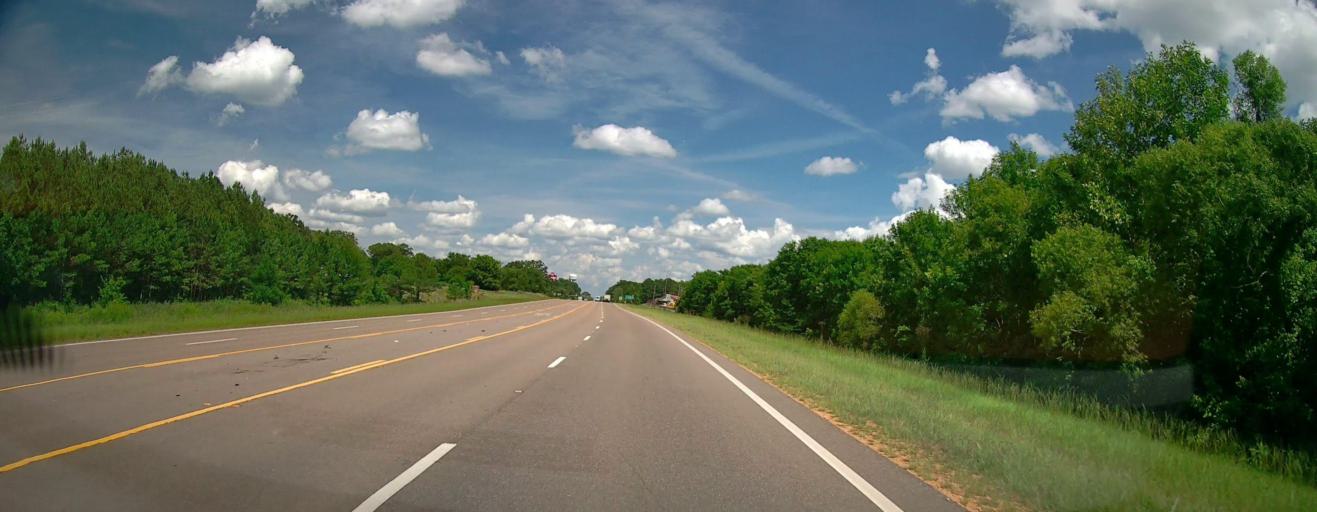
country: US
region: Mississippi
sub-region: Monroe County
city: Aberdeen
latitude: 33.8148
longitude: -88.5707
